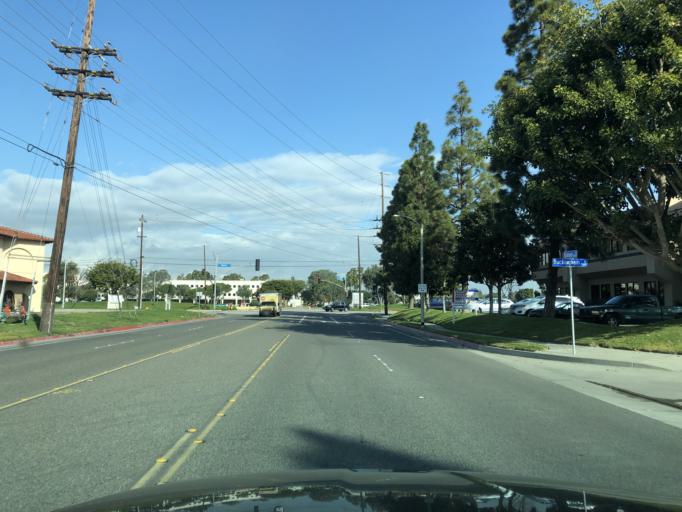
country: US
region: California
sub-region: Orange County
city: Westminster
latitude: 33.7434
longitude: -118.0328
